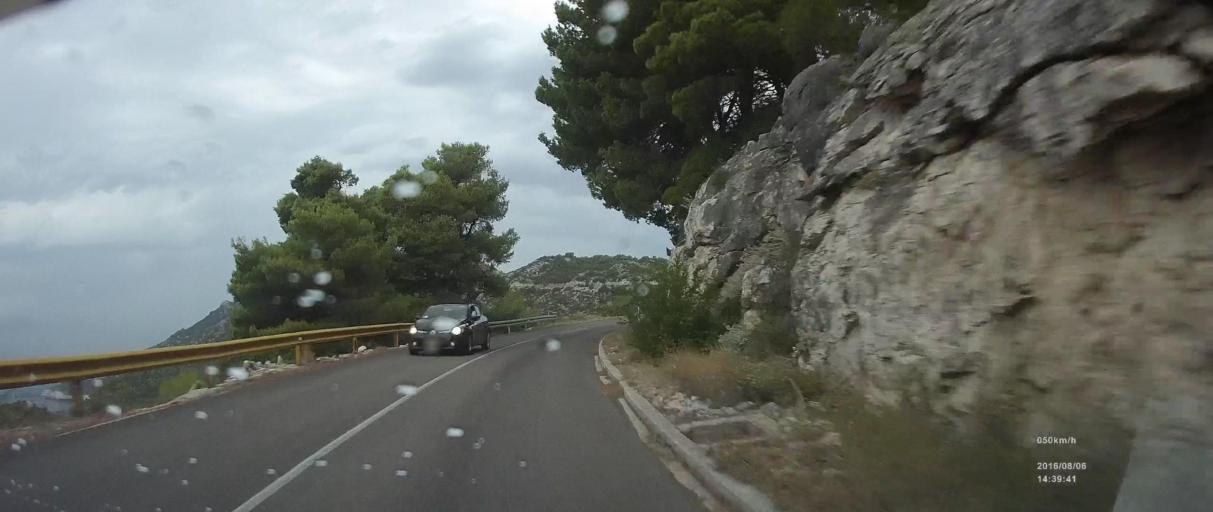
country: HR
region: Dubrovacko-Neretvanska
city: Ston
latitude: 42.7175
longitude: 17.6593
